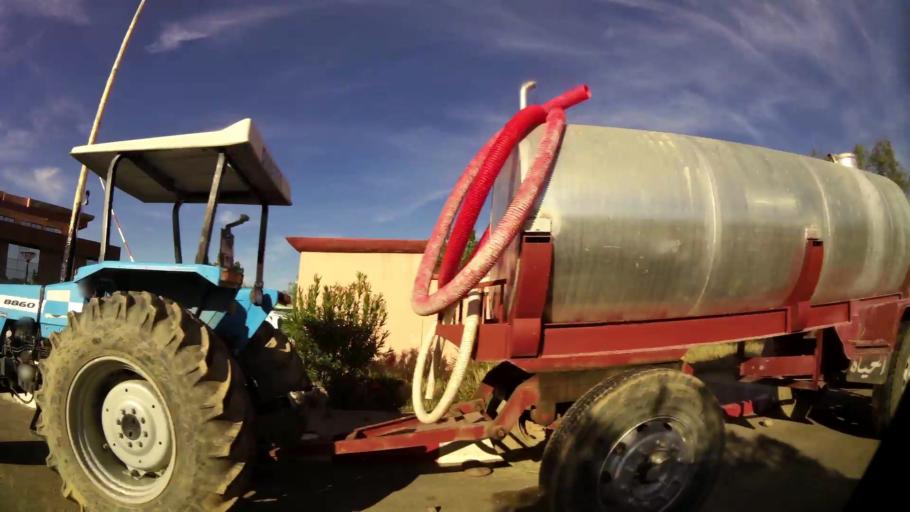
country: MA
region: Marrakech-Tensift-Al Haouz
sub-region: Marrakech
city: Marrakesh
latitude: 31.7528
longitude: -8.1096
